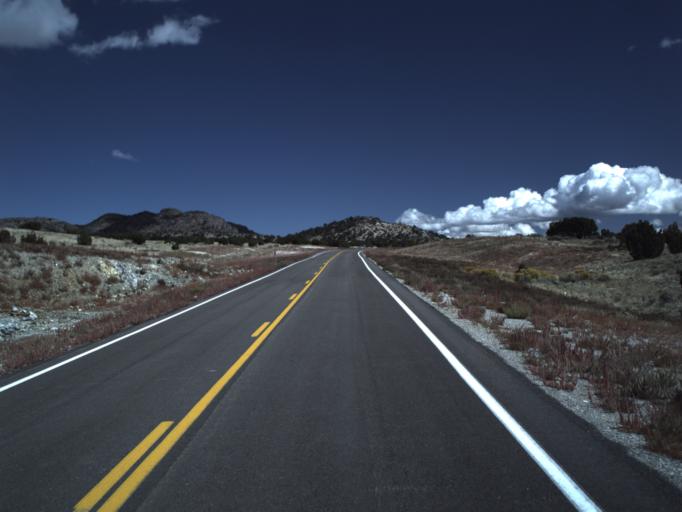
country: US
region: Utah
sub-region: Beaver County
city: Milford
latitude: 38.5169
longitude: -113.5524
